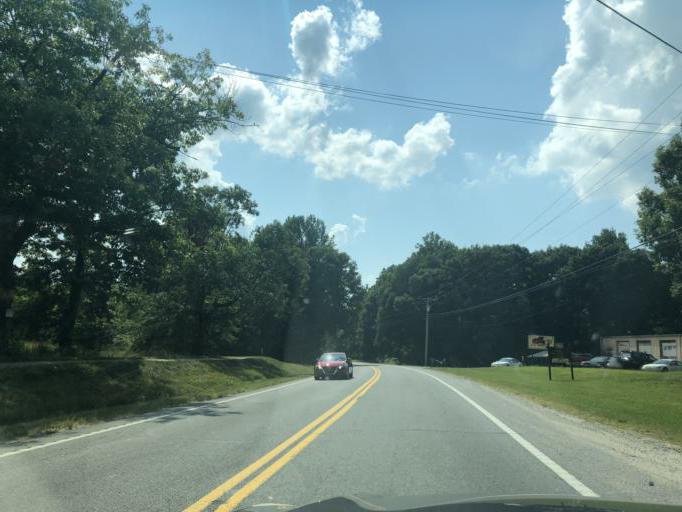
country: US
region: Tennessee
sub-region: Marion County
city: Monteagle
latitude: 35.2236
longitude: -85.8733
